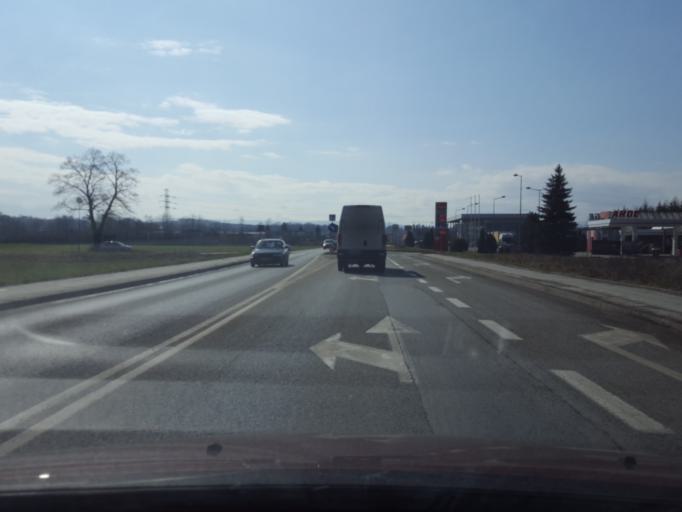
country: PL
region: Lesser Poland Voivodeship
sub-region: Powiat nowosadecki
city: Chelmiec
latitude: 49.6604
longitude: 20.6892
